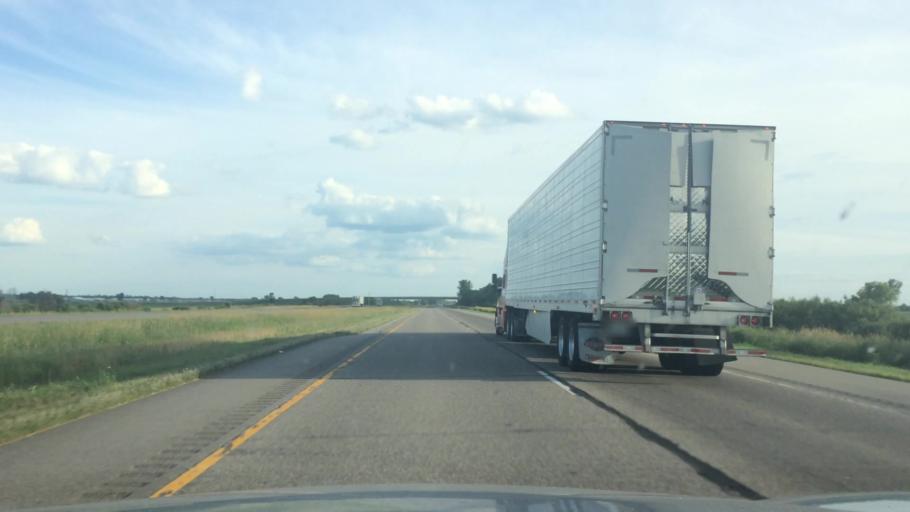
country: US
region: Wisconsin
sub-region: Portage County
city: Plover
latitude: 44.3734
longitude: -89.5200
